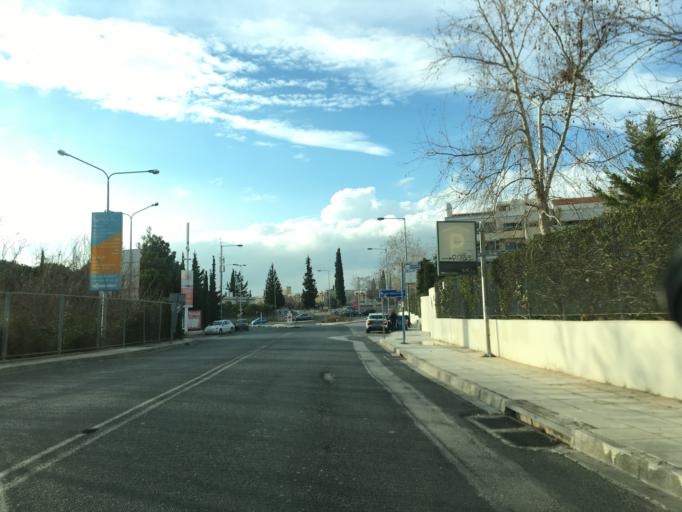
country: GR
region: Attica
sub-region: Nomarchia Athinas
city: Marousi
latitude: 38.0417
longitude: 23.7901
